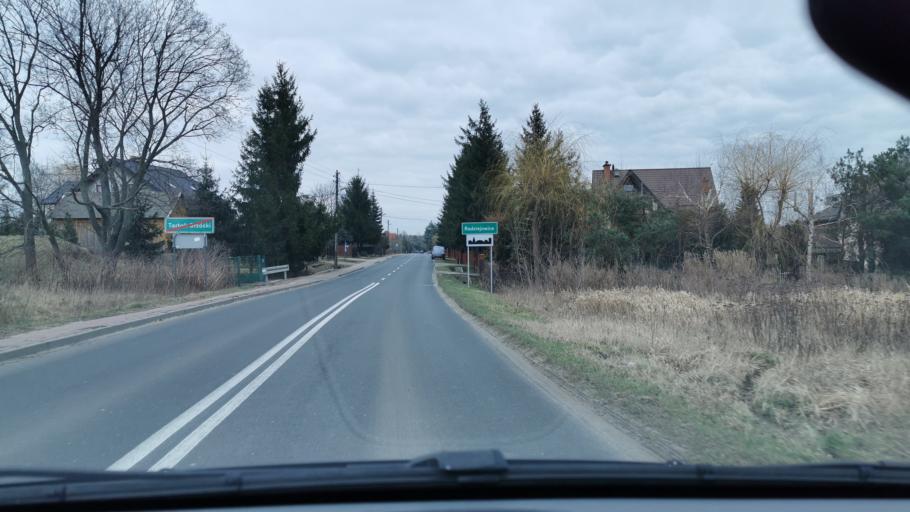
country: PL
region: Masovian Voivodeship
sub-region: Powiat zyrardowski
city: Radziejowice
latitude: 52.0098
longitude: 20.5387
